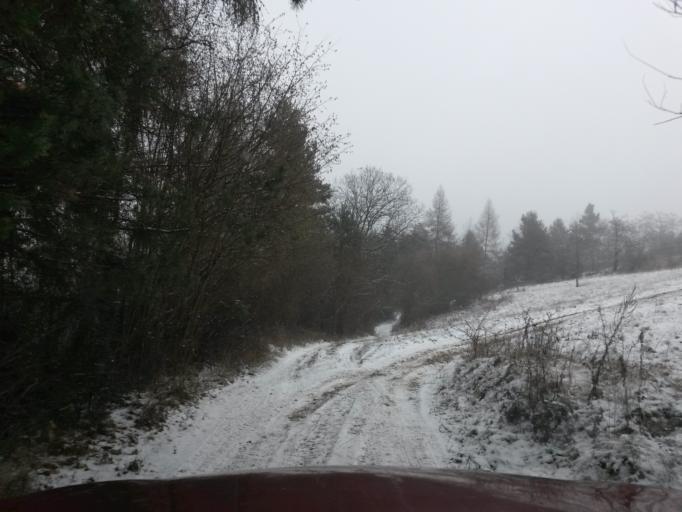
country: SK
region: Kosicky
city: Krompachy
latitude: 48.9831
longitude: 20.9873
